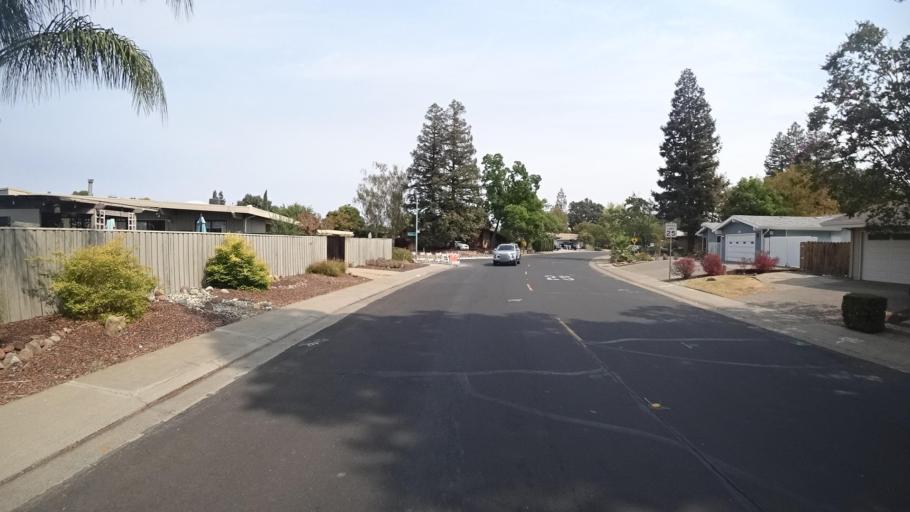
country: US
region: California
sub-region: Sacramento County
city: Elk Grove
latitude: 38.4154
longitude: -121.3791
